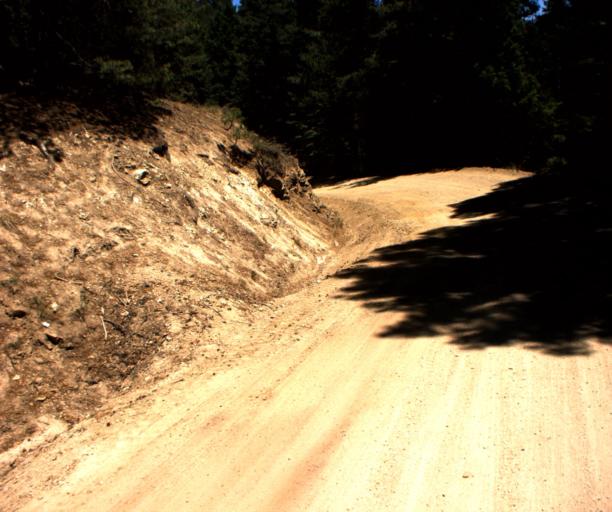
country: US
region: Arizona
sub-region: Graham County
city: Swift Trail Junction
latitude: 32.6828
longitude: -109.8961
